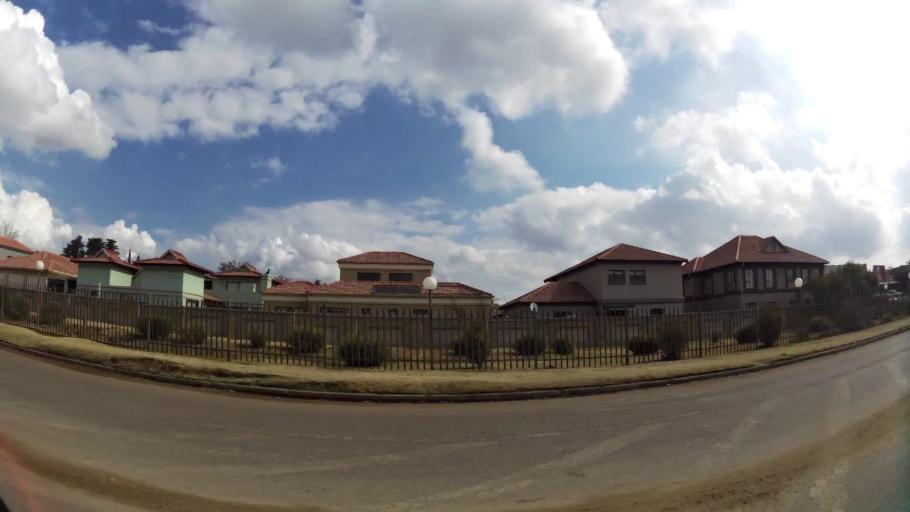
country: ZA
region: Gauteng
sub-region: Sedibeng District Municipality
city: Vanderbijlpark
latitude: -26.7344
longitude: 27.8377
